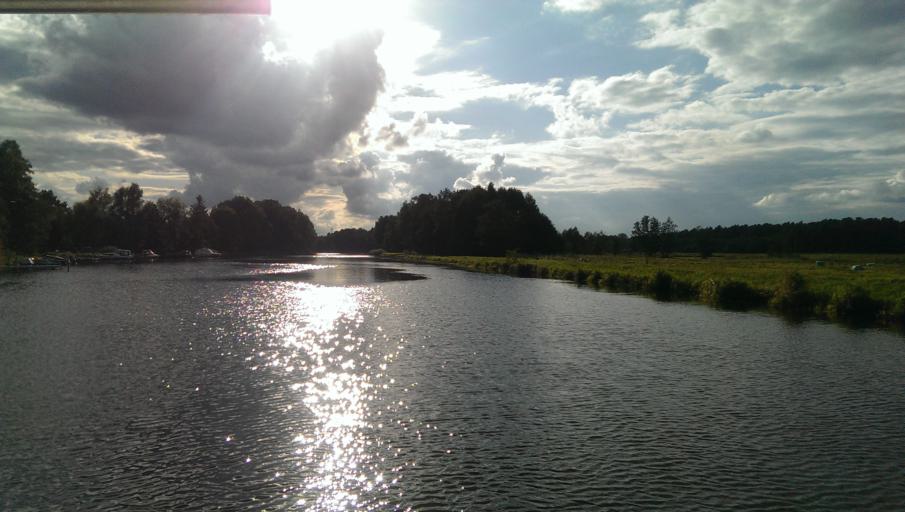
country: DE
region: Brandenburg
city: Liebenwalde
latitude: 52.8197
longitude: 13.3326
